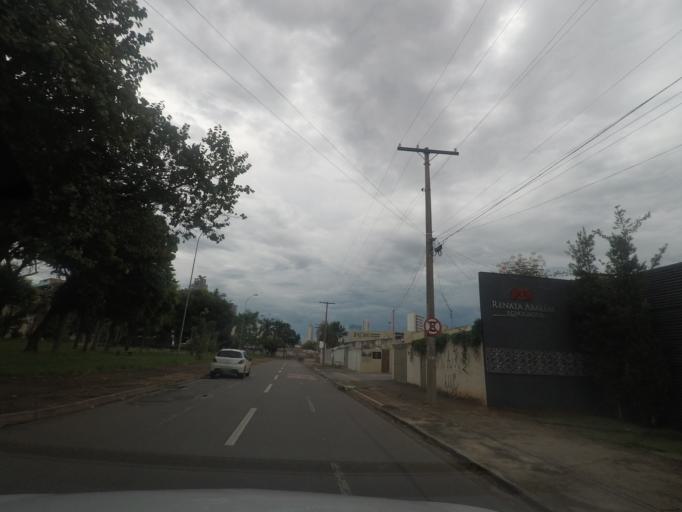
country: BR
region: Goias
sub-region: Goiania
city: Goiania
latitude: -16.6877
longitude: -49.2580
